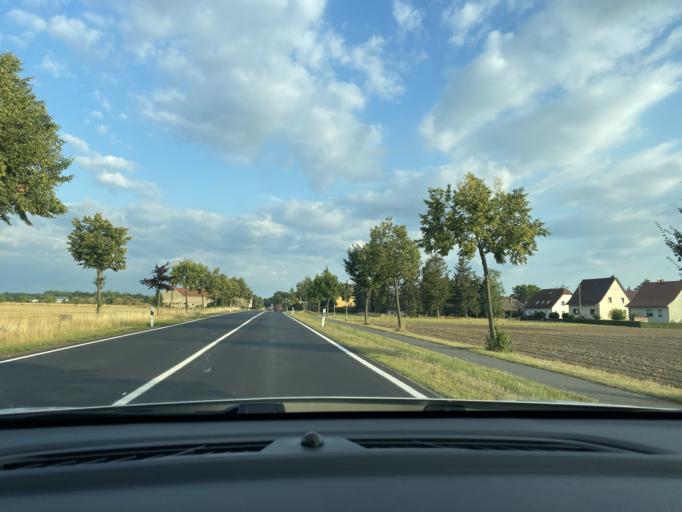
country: DE
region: Saxony
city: Neschwitz
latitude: 51.2769
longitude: 14.3388
